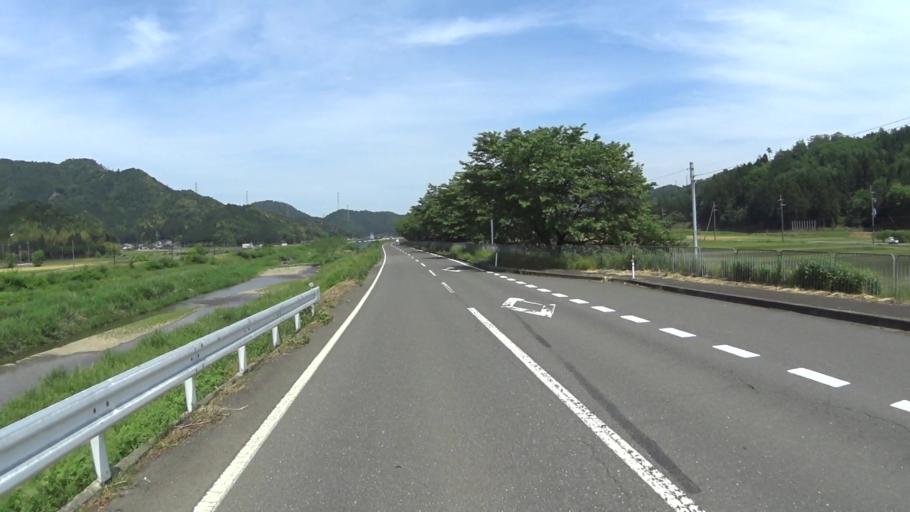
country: JP
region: Fukui
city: Obama
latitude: 35.4535
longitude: 135.5738
